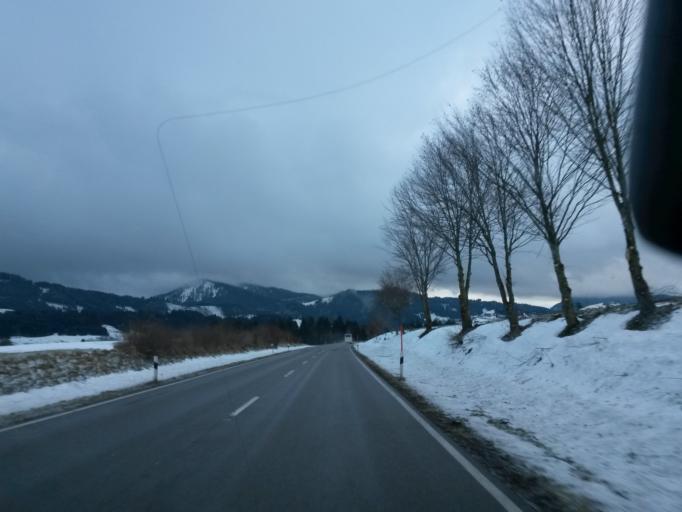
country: DE
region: Bavaria
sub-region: Swabia
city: Oy-Mittelberg
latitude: 47.6129
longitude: 10.4329
